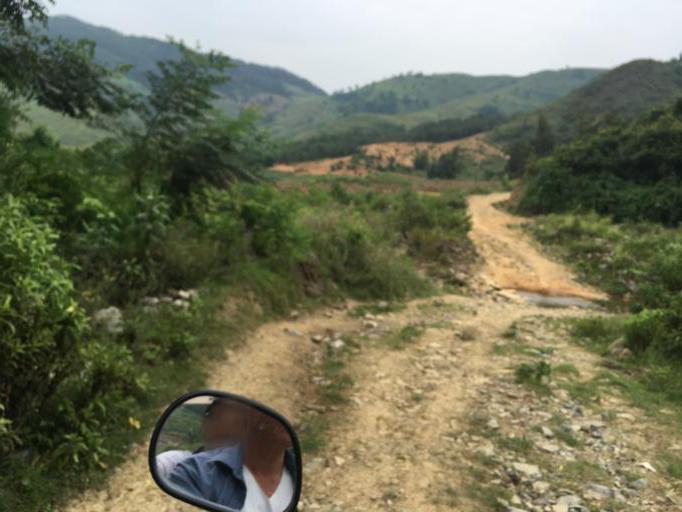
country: CN
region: Guizhou Sheng
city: Anshun
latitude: 25.4791
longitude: 105.9295
